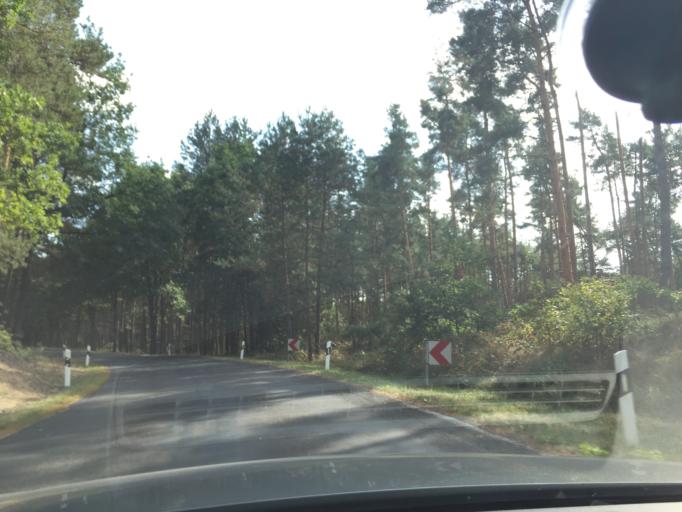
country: DE
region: Brandenburg
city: Grunheide
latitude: 52.3667
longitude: 13.8213
